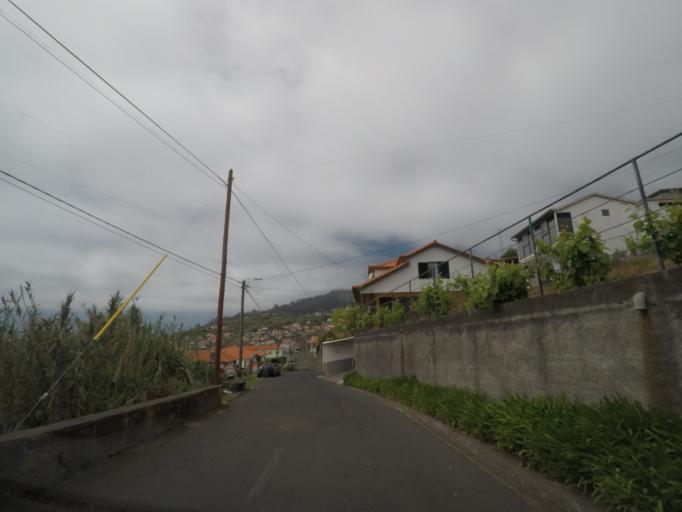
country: PT
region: Madeira
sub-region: Calheta
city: Arco da Calheta
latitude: 32.7112
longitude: -17.1192
